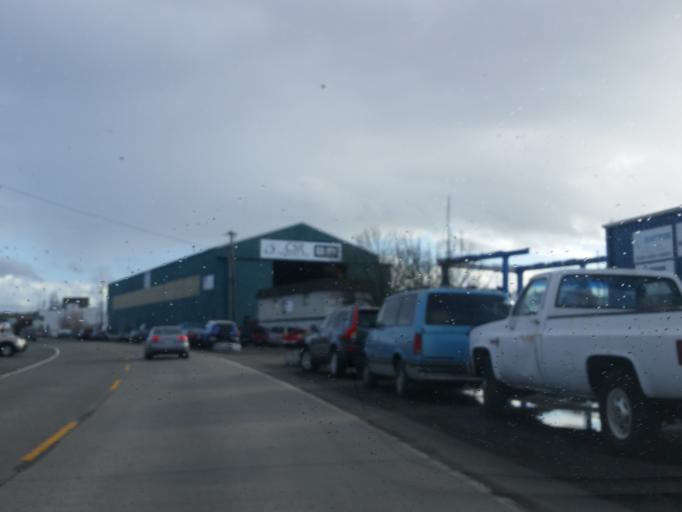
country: US
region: Washington
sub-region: King County
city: Seattle
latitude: 47.6631
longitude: -122.3807
